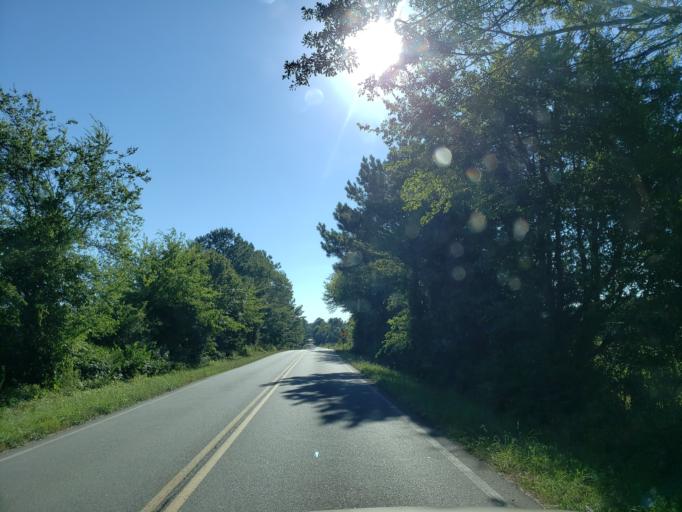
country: US
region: Georgia
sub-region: Bartow County
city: Euharlee
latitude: 34.1044
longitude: -84.9878
